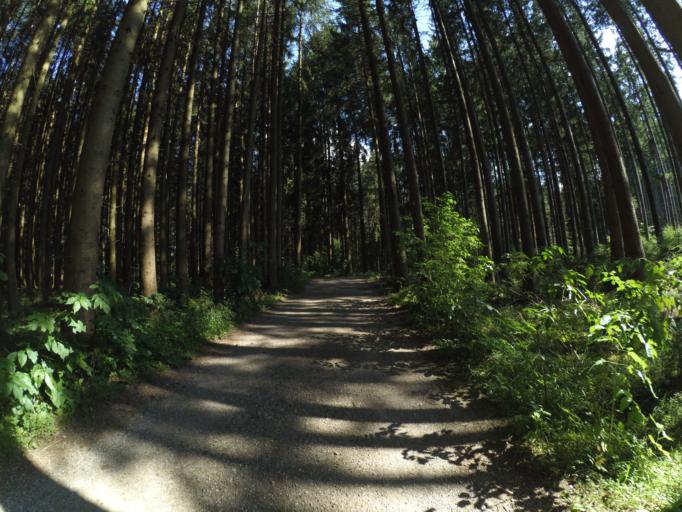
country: DE
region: Bavaria
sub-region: Swabia
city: Bad Worishofen
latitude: 47.9925
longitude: 10.5790
